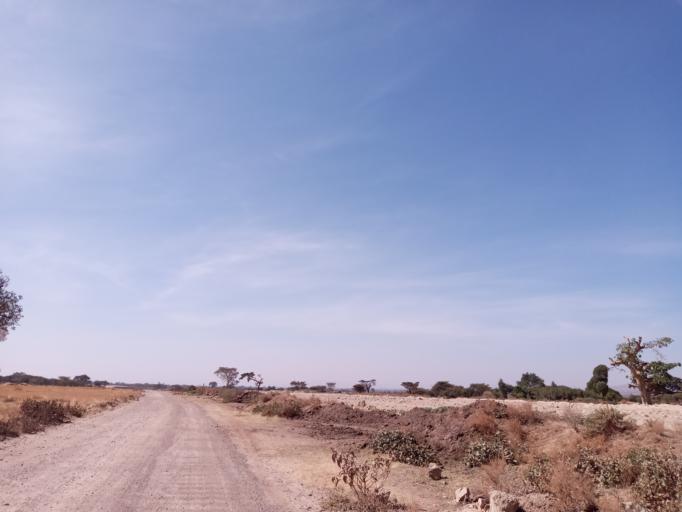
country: ET
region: Oromiya
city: Shashemene
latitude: 7.3856
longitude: 38.6504
